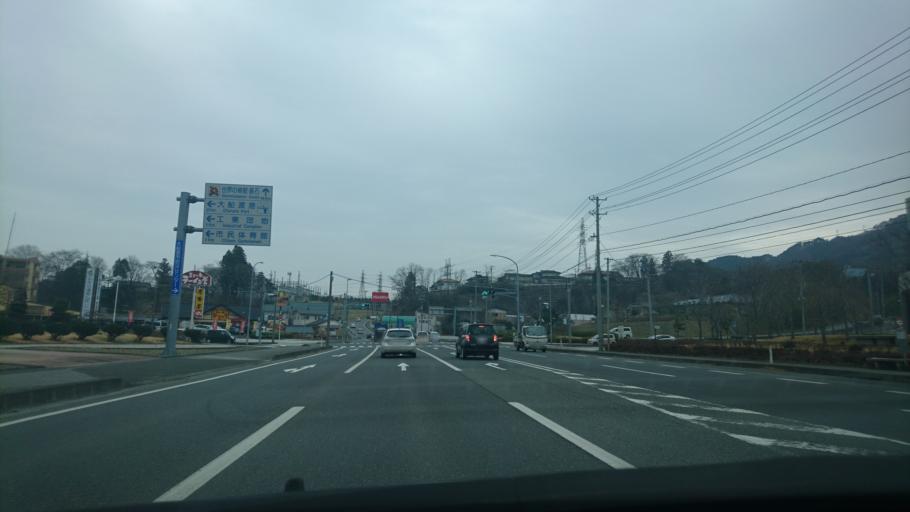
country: JP
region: Iwate
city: Ofunato
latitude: 39.0786
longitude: 141.7112
